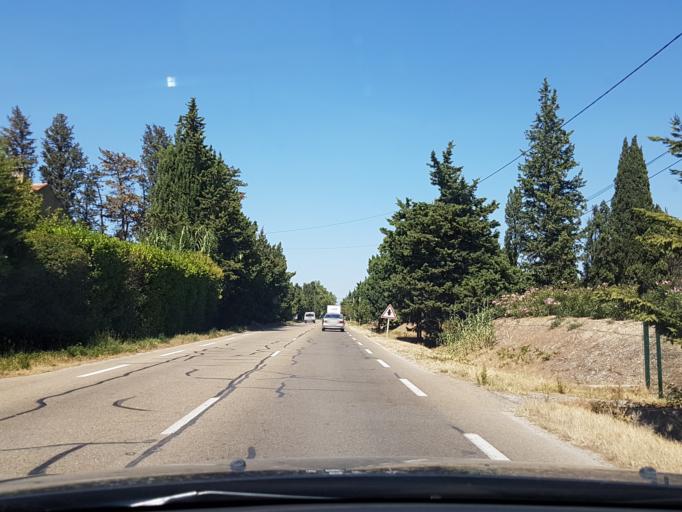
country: FR
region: Provence-Alpes-Cote d'Azur
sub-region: Departement des Bouches-du-Rhone
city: Chateaurenard
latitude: 43.8726
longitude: 4.8355
